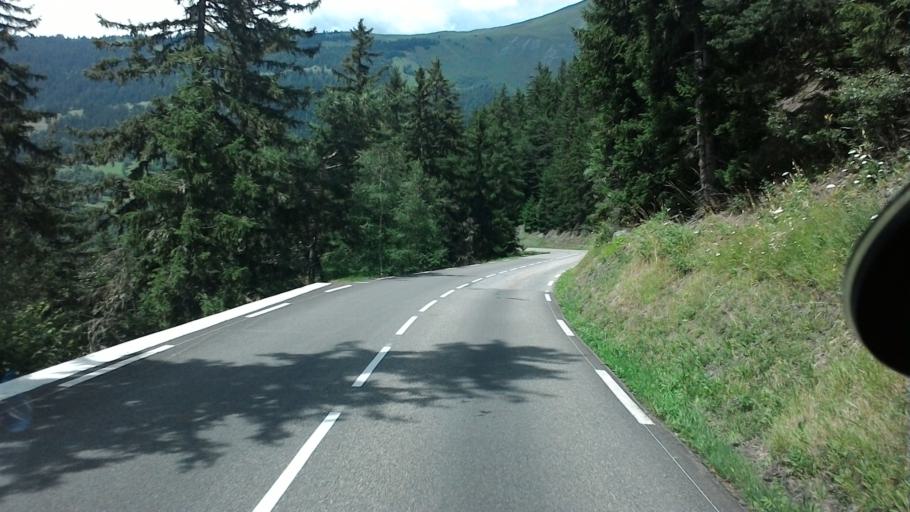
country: FR
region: Rhone-Alpes
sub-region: Departement de la Savoie
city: Seez
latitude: 45.6278
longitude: 6.8241
